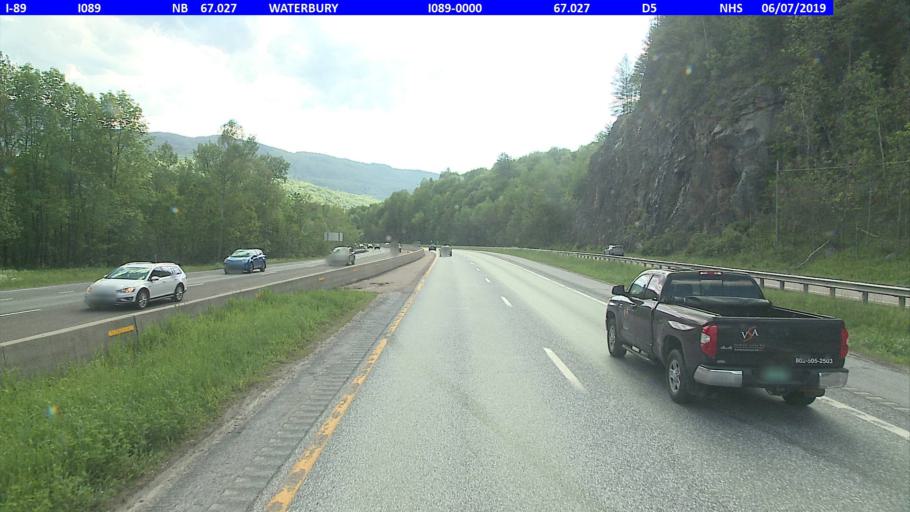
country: US
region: Vermont
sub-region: Washington County
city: Waterbury
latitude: 44.3602
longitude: -72.8092
